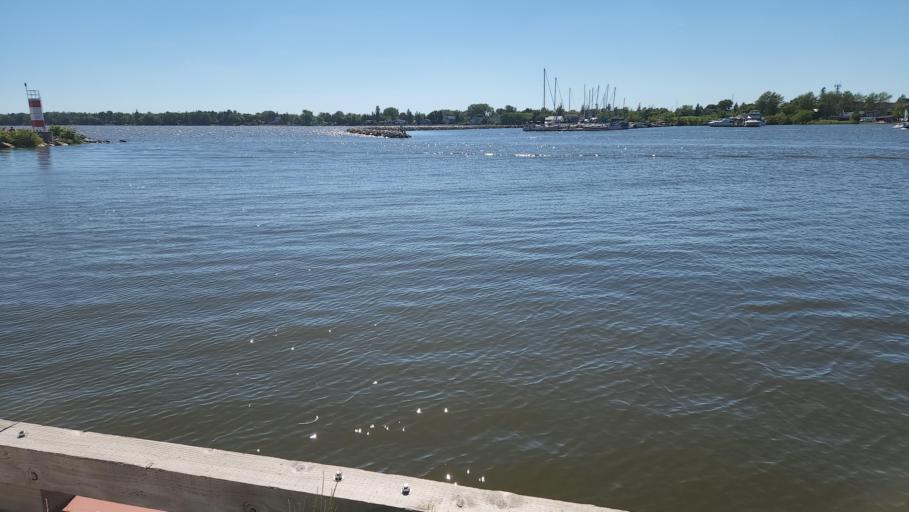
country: CA
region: Manitoba
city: Gimli
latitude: 50.6299
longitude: -96.9803
